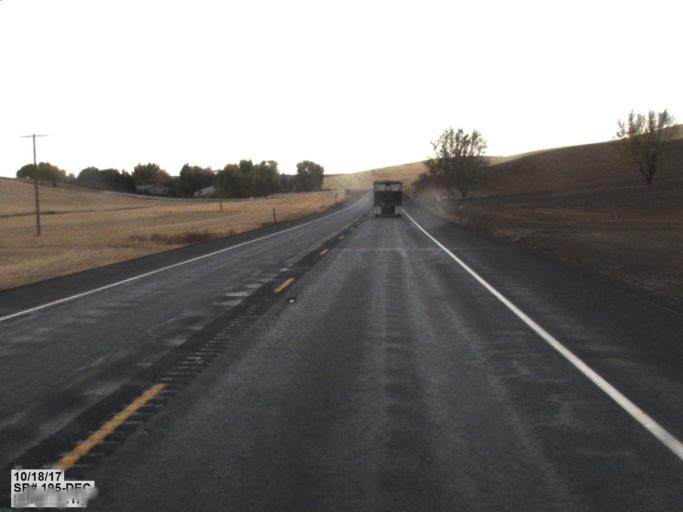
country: US
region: Washington
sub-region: Whitman County
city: Pullman
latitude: 46.6961
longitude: -117.2041
